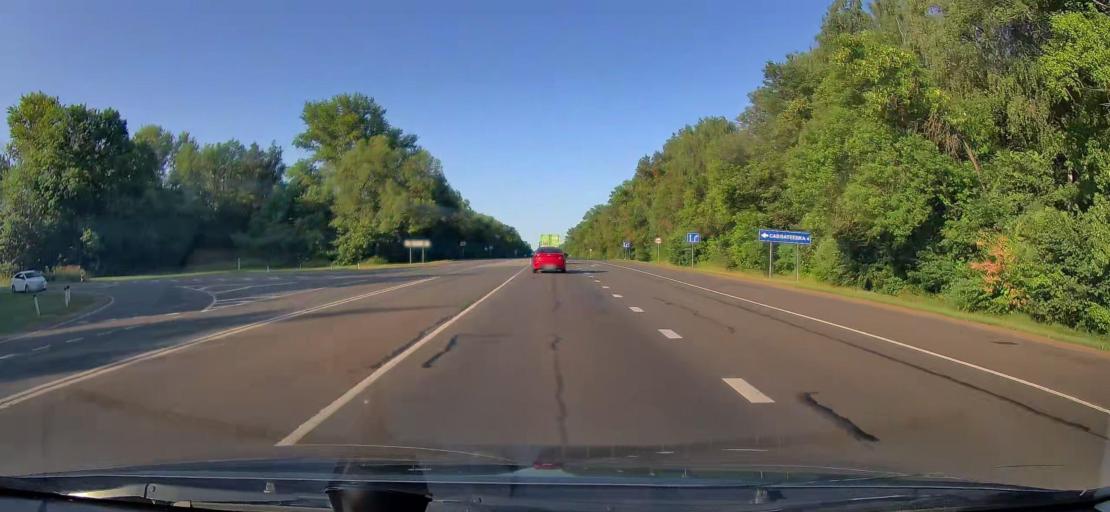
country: RU
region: Tula
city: Plavsk
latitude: 53.5976
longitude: 37.1641
